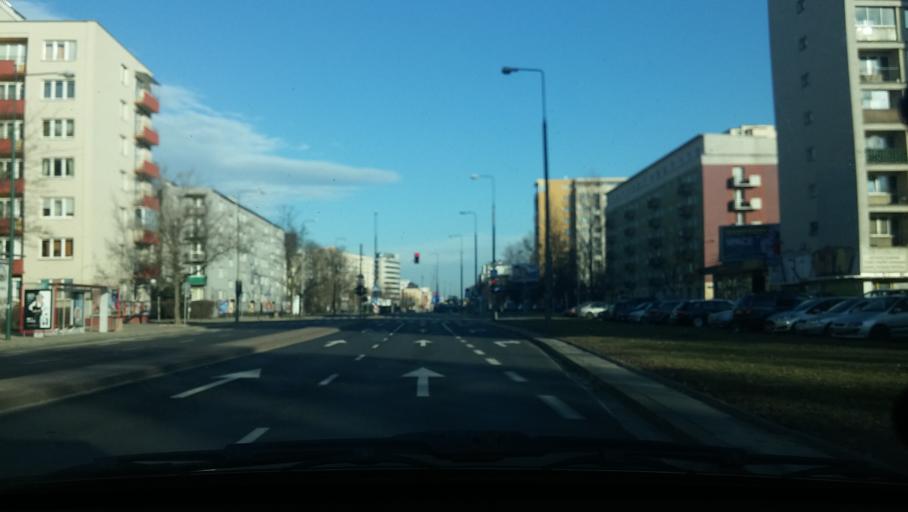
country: PL
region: Masovian Voivodeship
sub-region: Warszawa
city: Mokotow
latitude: 52.1861
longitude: 21.0189
